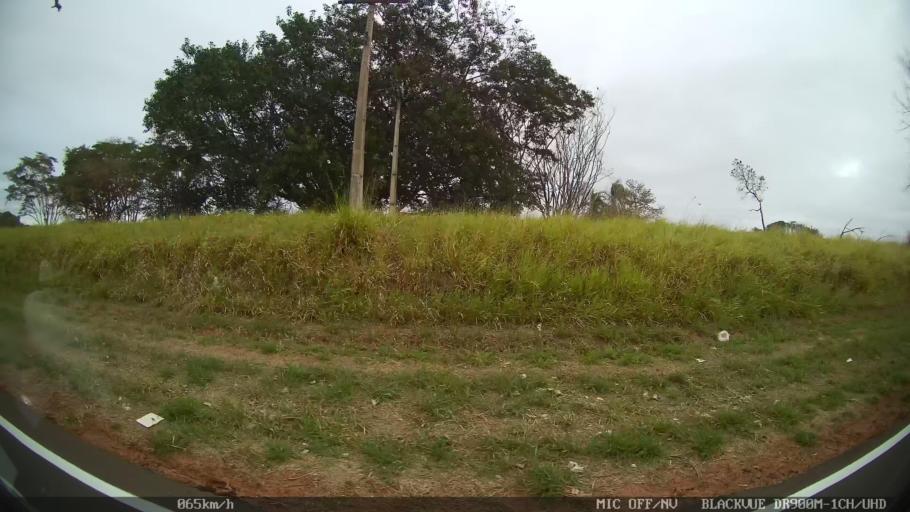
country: BR
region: Sao Paulo
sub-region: Sao Jose Do Rio Preto
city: Sao Jose do Rio Preto
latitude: -20.8291
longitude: -49.4256
